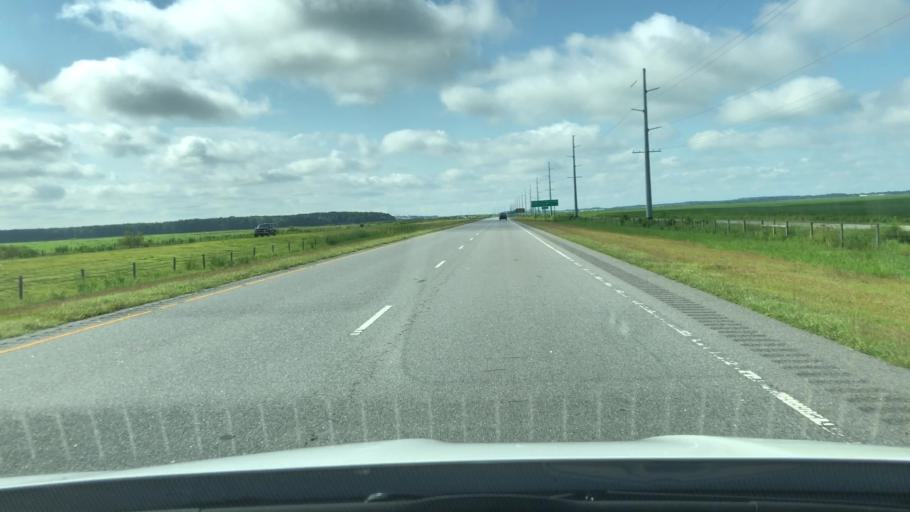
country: US
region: North Carolina
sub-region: Pasquotank County
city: Elizabeth City
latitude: 36.3163
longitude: -76.3084
